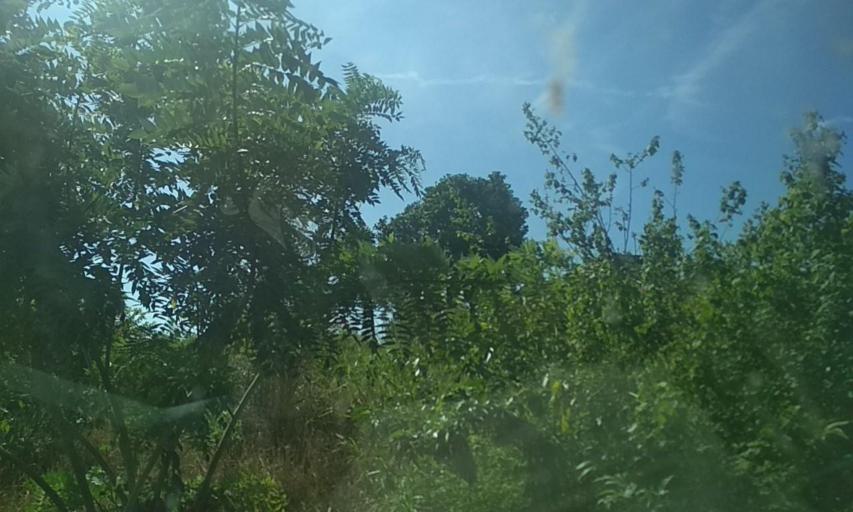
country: MX
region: Veracruz
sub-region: Martinez de la Torre
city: La Union Paso Largo
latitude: 20.1318
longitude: -96.9892
